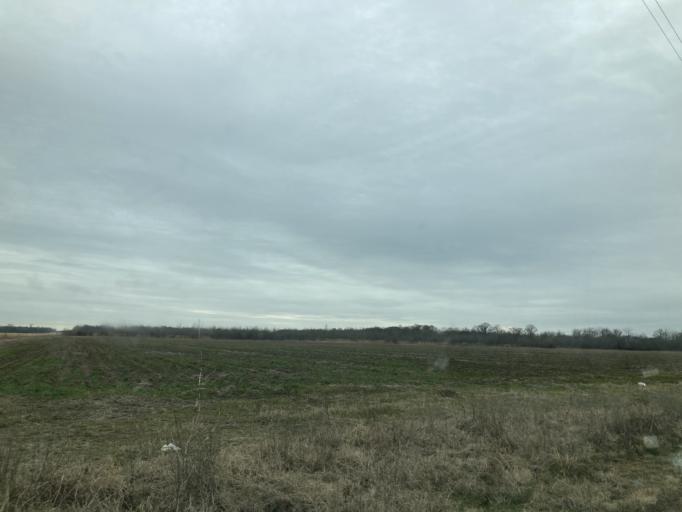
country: US
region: Mississippi
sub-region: Humphreys County
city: Belzoni
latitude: 33.0705
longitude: -90.4746
